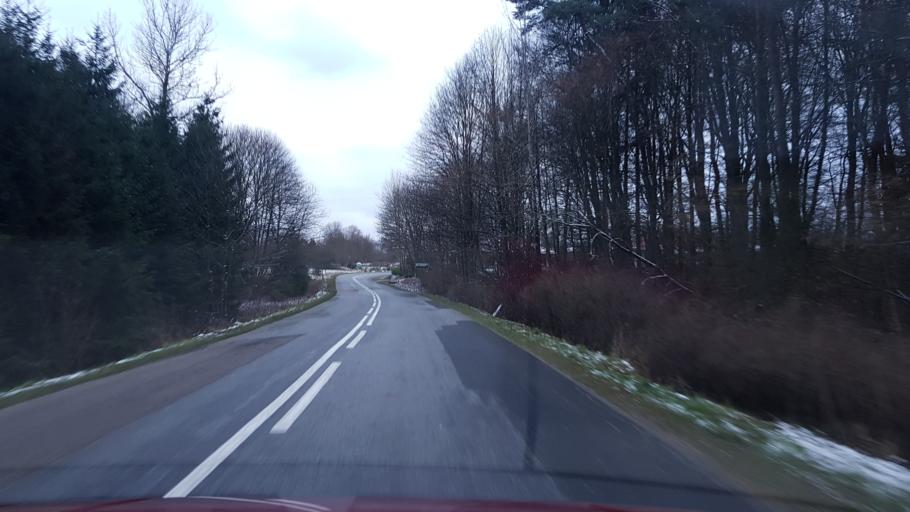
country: PL
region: Pomeranian Voivodeship
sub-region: Powiat bytowski
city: Miastko
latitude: 54.0243
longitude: 16.9481
